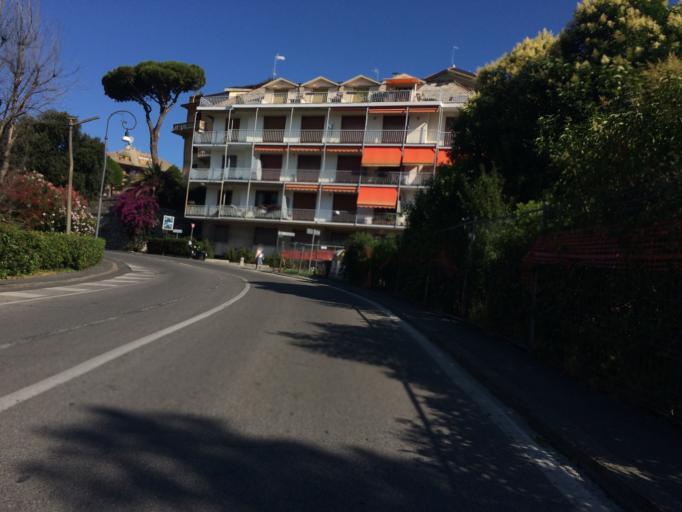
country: IT
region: Liguria
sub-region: Provincia di Genova
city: Rapallo
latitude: 44.3480
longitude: 9.2379
